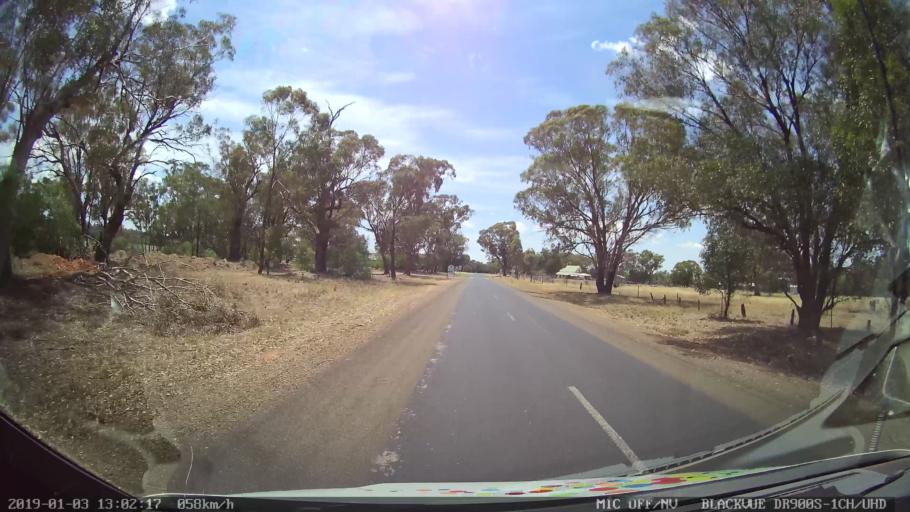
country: AU
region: New South Wales
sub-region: Cabonne
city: Canowindra
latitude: -33.6187
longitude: 148.4276
